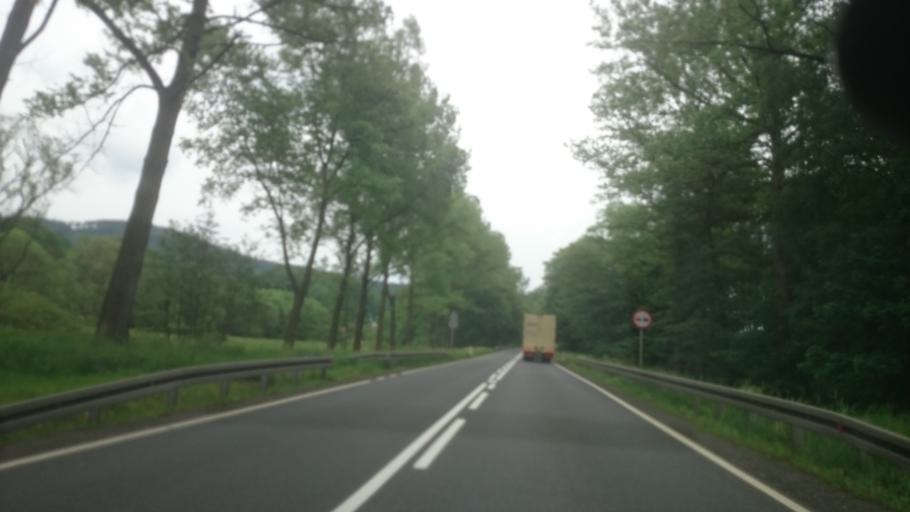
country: PL
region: Lower Silesian Voivodeship
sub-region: Powiat zabkowicki
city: Bardo
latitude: 50.4317
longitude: 16.7373
